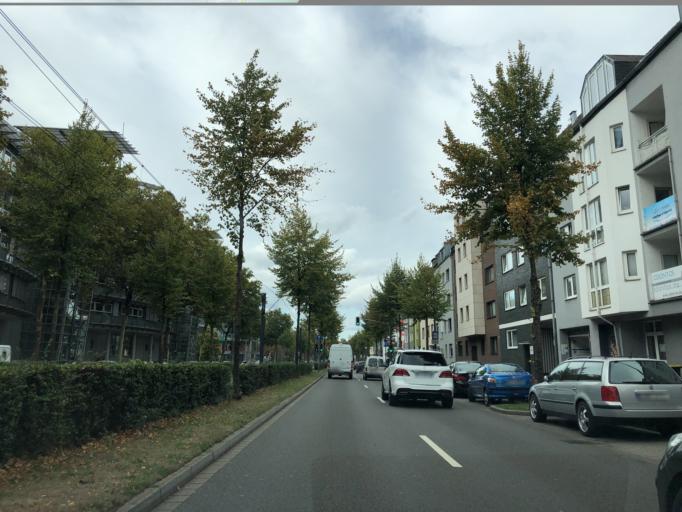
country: DE
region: North Rhine-Westphalia
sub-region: Regierungsbezirk Dusseldorf
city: Dusseldorf
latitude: 51.1949
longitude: 6.8137
